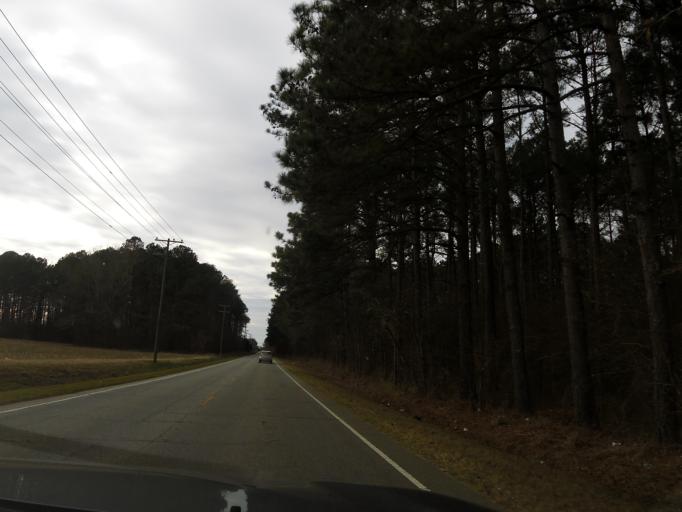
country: US
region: North Carolina
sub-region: Nash County
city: Rocky Mount
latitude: 35.9629
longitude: -77.6640
